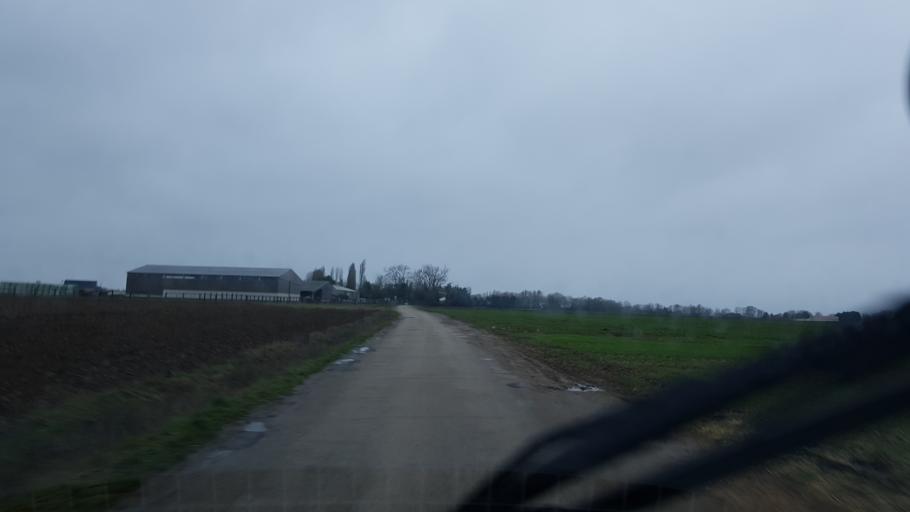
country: FR
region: Ile-de-France
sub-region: Departement de l'Essonne
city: Limours
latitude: 48.6529
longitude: 2.0990
